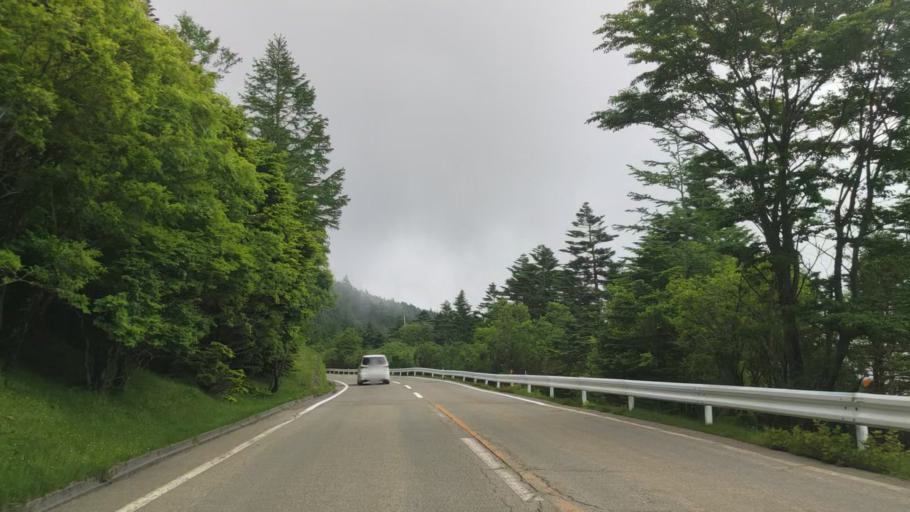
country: JP
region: Yamanashi
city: Fujikawaguchiko
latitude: 35.3970
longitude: 138.6920
